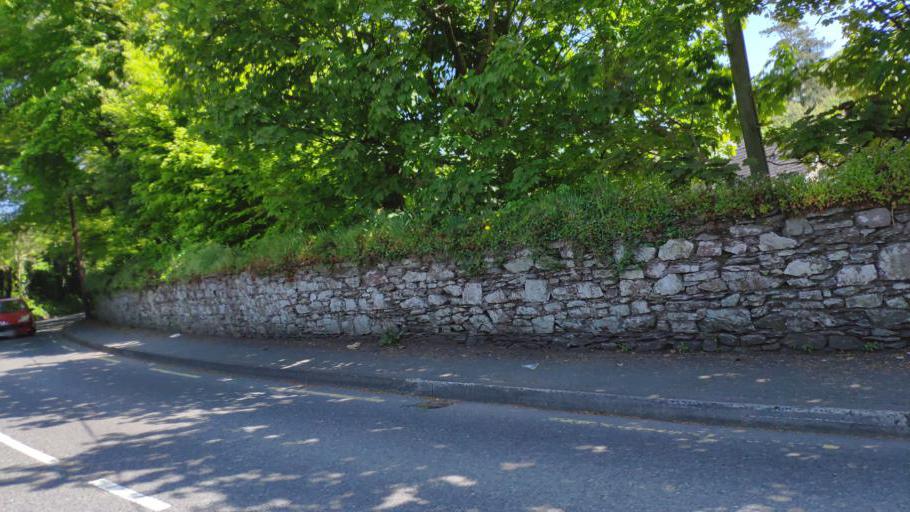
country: IE
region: Munster
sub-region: County Cork
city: Cork
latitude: 51.9255
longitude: -8.4911
